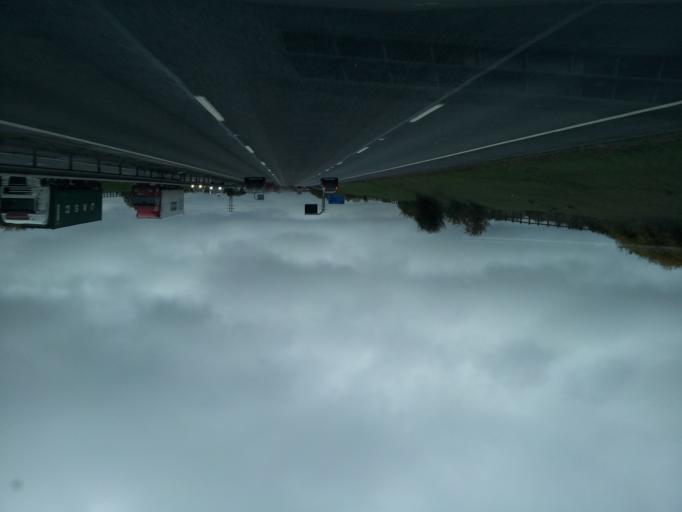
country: GB
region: England
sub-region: Oxfordshire
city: Bicester
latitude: 51.9116
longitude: -1.2049
